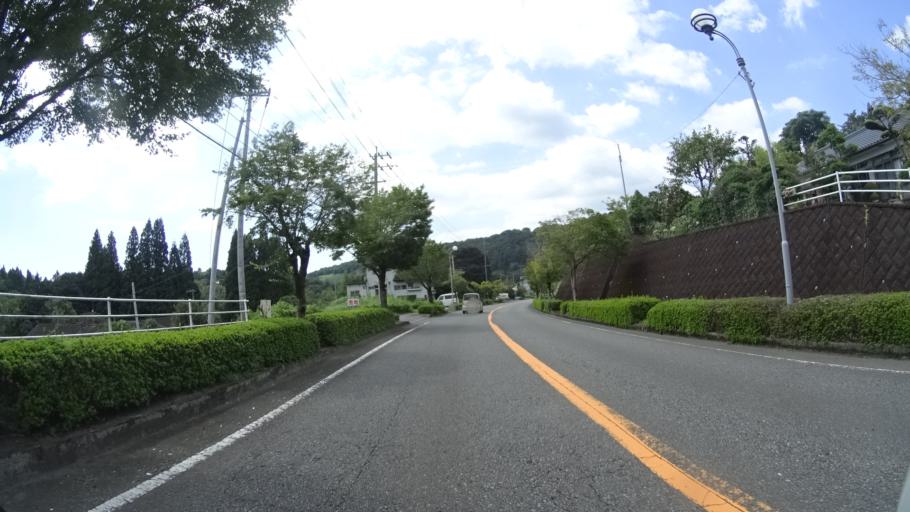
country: JP
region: Kagoshima
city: Kokubu-matsuki
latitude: 31.8843
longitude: 130.8071
